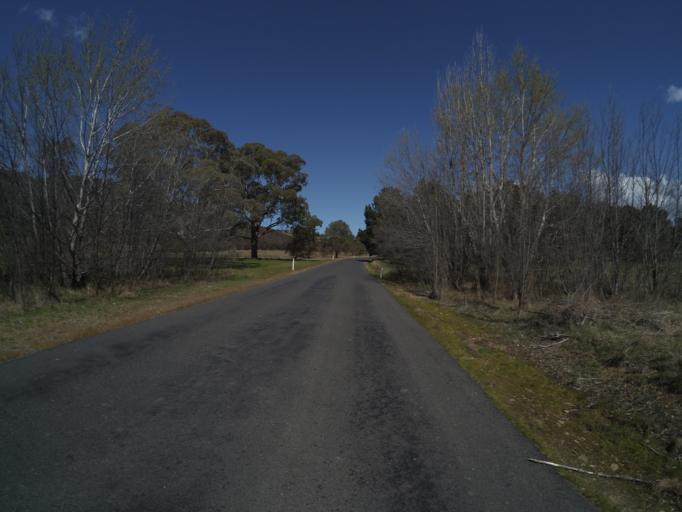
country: AU
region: Australian Capital Territory
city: Macquarie
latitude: -35.1652
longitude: 148.8865
